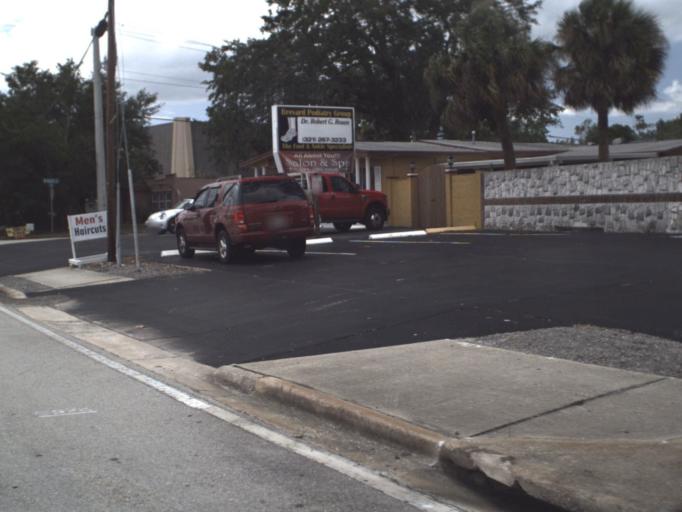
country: US
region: Florida
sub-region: Brevard County
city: Titusville
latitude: 28.6155
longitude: -80.8142
